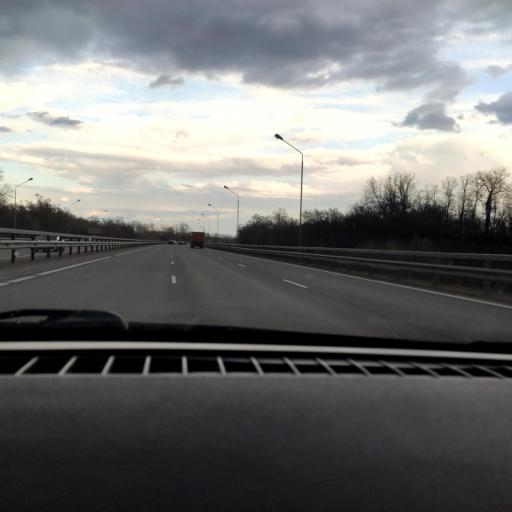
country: RU
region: Bashkortostan
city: Ufa
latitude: 54.6595
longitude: 55.8808
